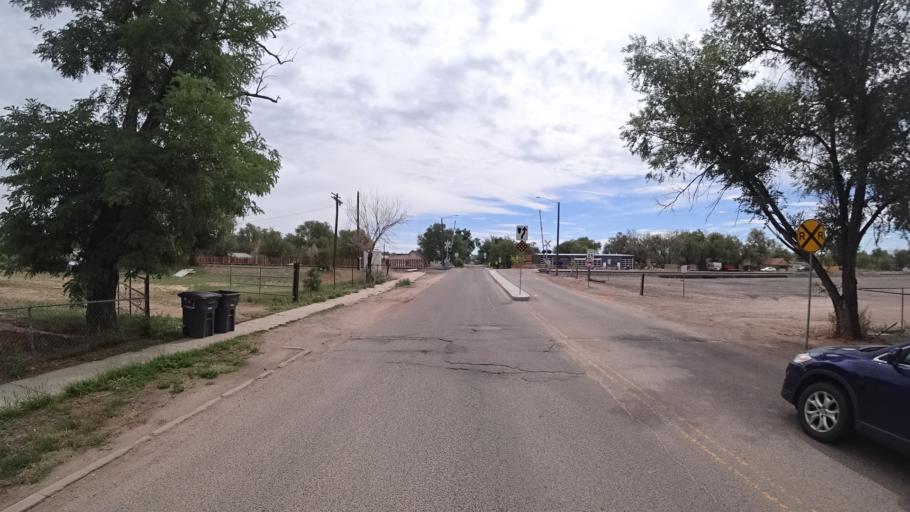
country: US
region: Colorado
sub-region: El Paso County
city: Fountain
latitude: 38.6808
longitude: -104.7039
